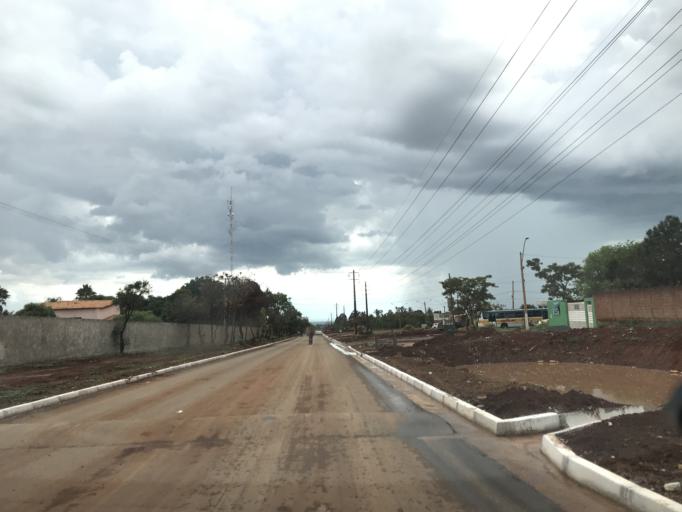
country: BR
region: Federal District
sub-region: Brasilia
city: Brasilia
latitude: -15.9688
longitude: -48.0456
